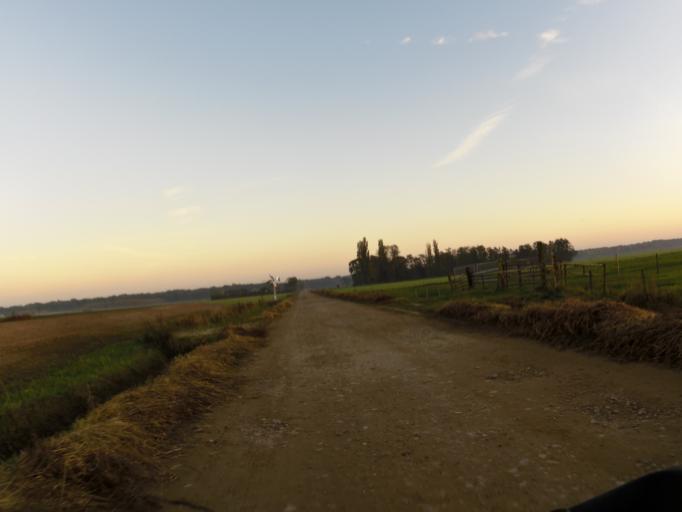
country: NL
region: North Brabant
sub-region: Gemeente Vught
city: Vught
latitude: 51.6780
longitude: 5.2737
